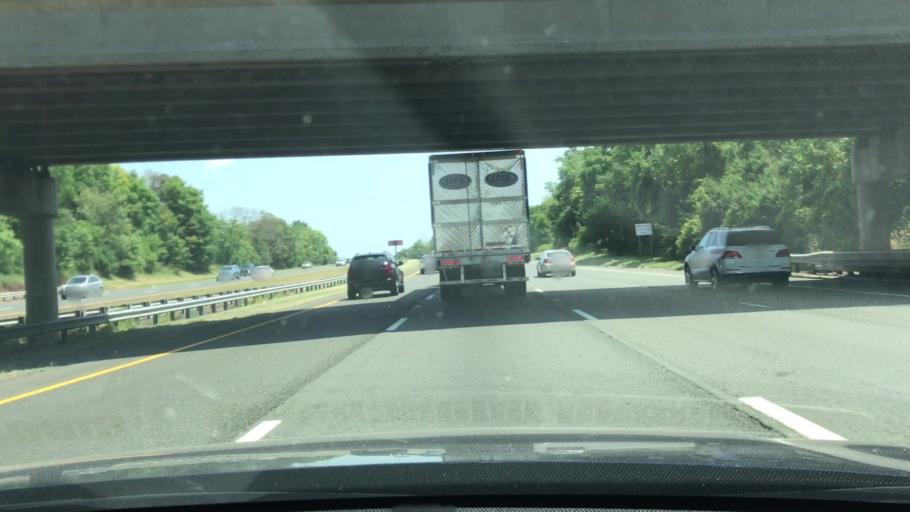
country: US
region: New Jersey
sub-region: Somerset County
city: South Bound Brook
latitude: 40.5474
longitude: -74.5384
